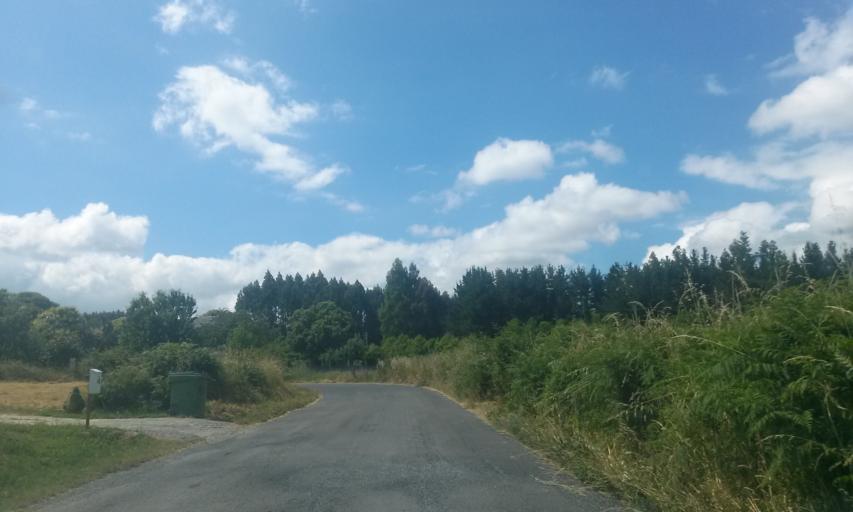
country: ES
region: Galicia
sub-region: Provincia de Lugo
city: Begonte
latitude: 43.1179
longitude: -7.6621
